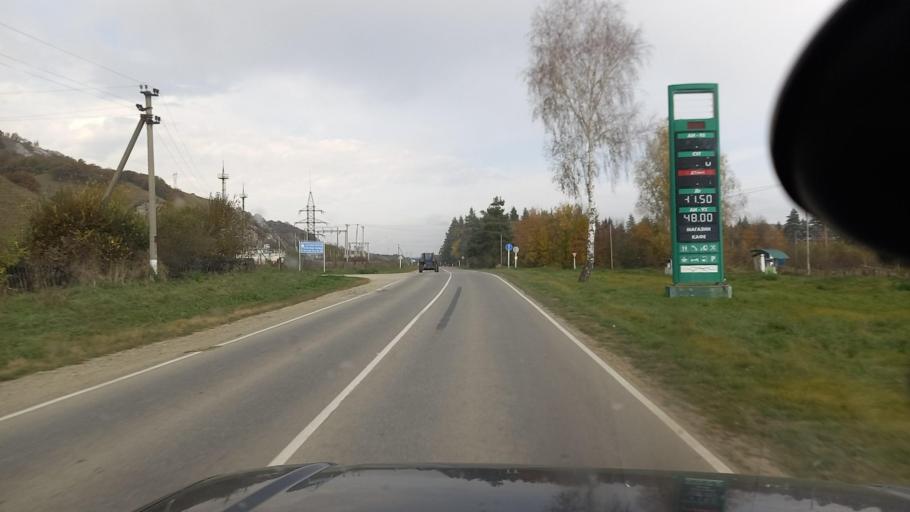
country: RU
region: Krasnodarskiy
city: Psebay
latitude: 44.1473
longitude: 40.8274
